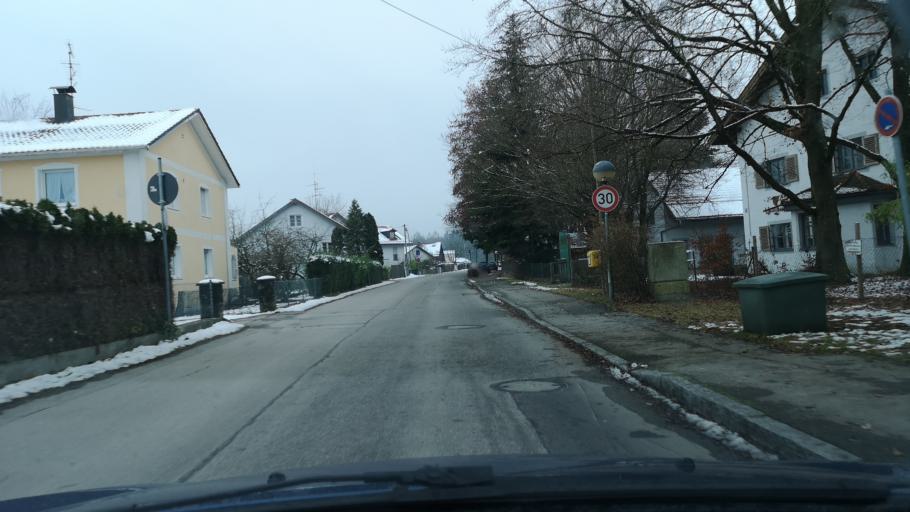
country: DE
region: Bavaria
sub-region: Upper Bavaria
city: Anzing
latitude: 48.1446
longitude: 11.8617
